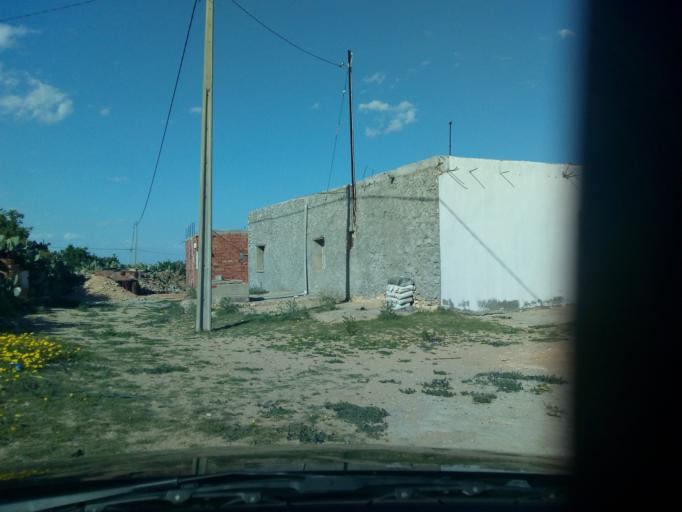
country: TN
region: Safaqis
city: Sfax
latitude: 34.7304
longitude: 10.6109
